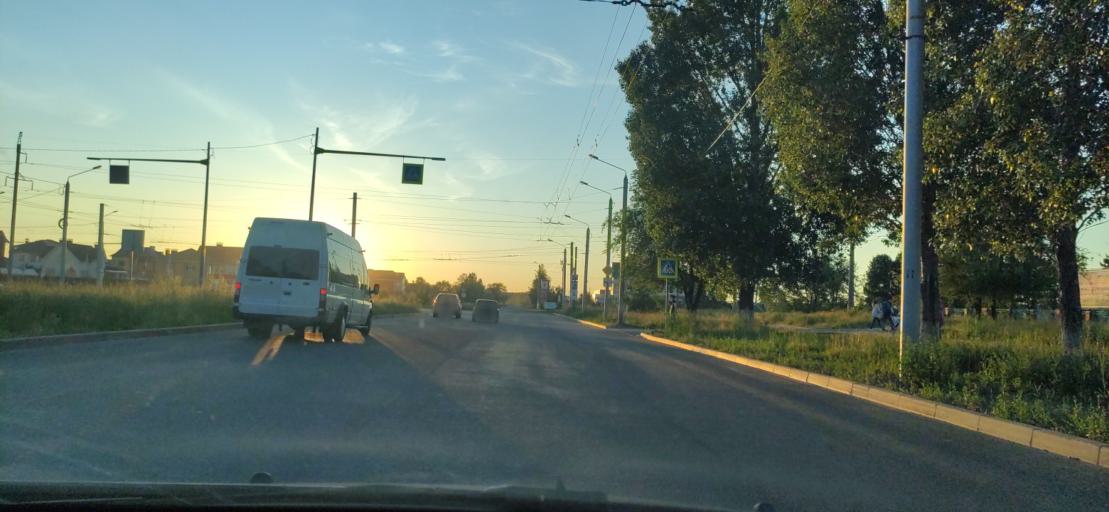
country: RU
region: Ulyanovsk
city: Mirnyy
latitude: 54.3881
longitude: 48.6130
